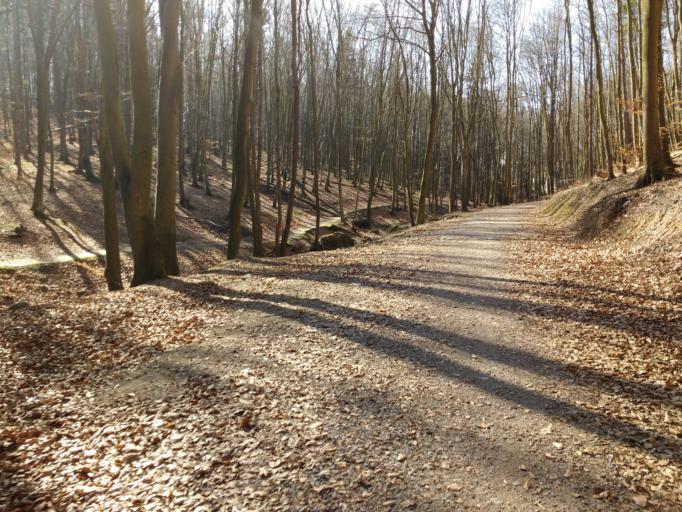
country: PL
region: Pomeranian Voivodeship
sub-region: Gdynia
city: Wielki Kack
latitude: 54.4806
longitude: 18.5151
